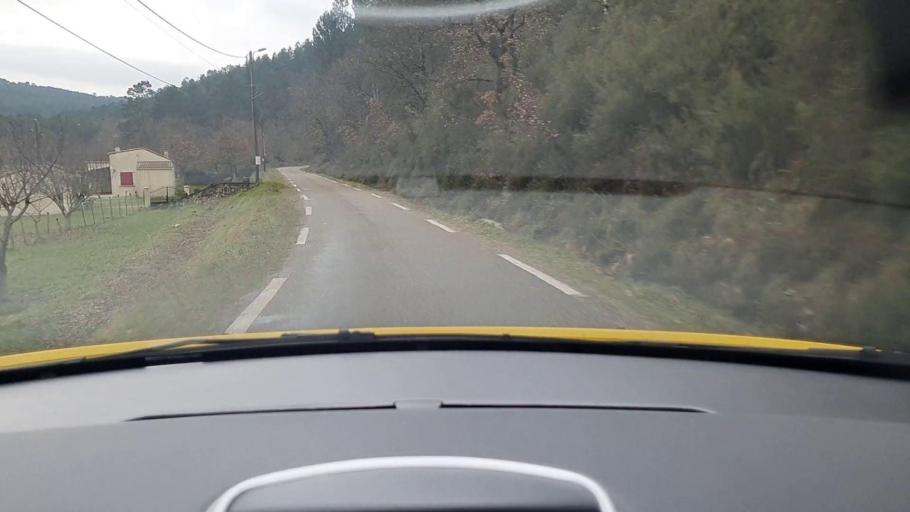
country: FR
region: Languedoc-Roussillon
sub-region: Departement du Gard
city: Besseges
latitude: 44.3251
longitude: 4.1196
